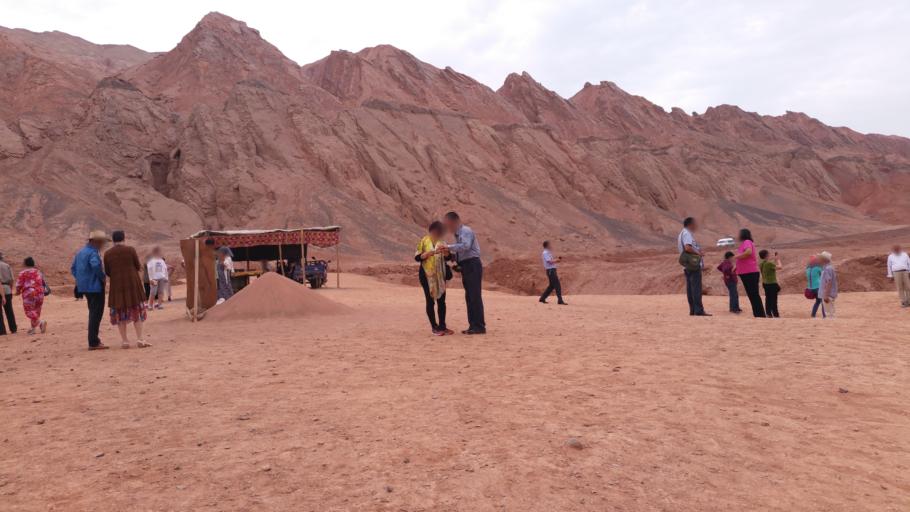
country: CN
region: Xinjiang Uygur Zizhiqu
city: Laochenglu
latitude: 42.9443
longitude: 89.5525
